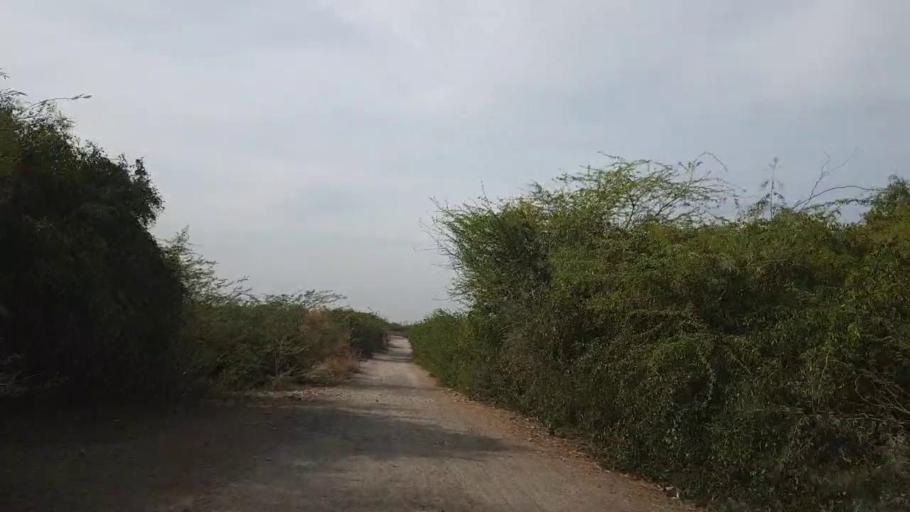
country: PK
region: Sindh
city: Nabisar
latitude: 24.9919
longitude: 69.5594
